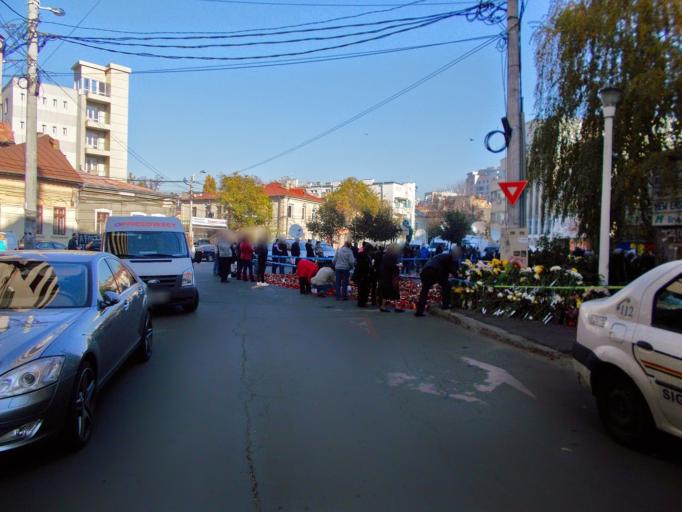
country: RO
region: Bucuresti
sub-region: Municipiul Bucuresti
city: Bucharest
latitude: 44.4208
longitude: 26.1076
